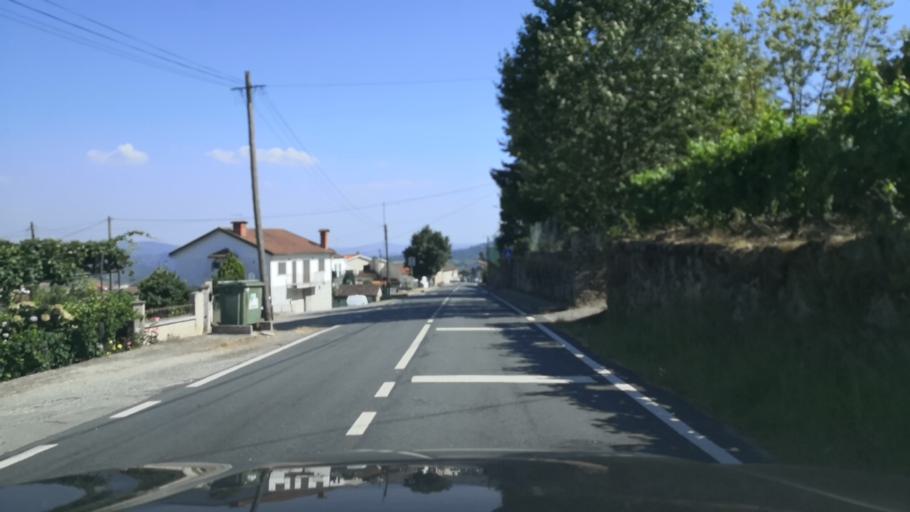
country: PT
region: Vila Real
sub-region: Sabrosa
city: Sabrosa
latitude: 41.2930
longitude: -7.4800
